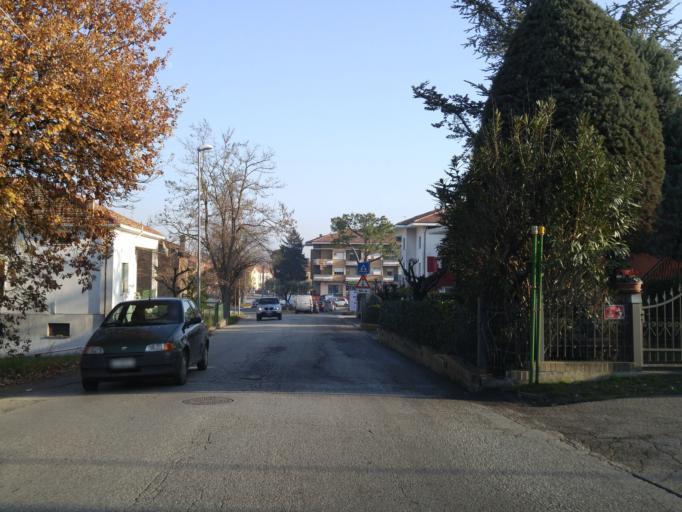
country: IT
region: The Marches
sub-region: Provincia di Pesaro e Urbino
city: Lucrezia
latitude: 43.7724
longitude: 12.9323
